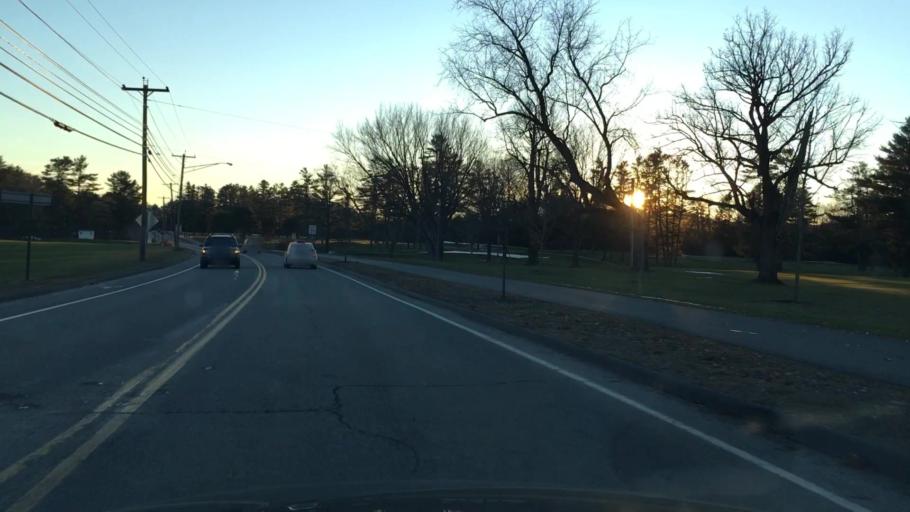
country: US
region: New Hampshire
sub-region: Grafton County
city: Hanover
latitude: 43.7178
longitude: -72.2745
